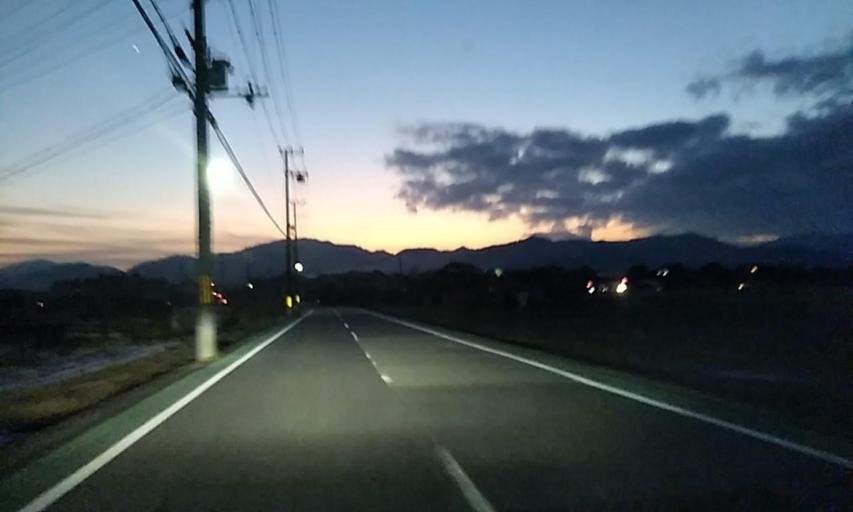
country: JP
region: Kyoto
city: Kameoka
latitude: 35.0138
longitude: 135.5620
